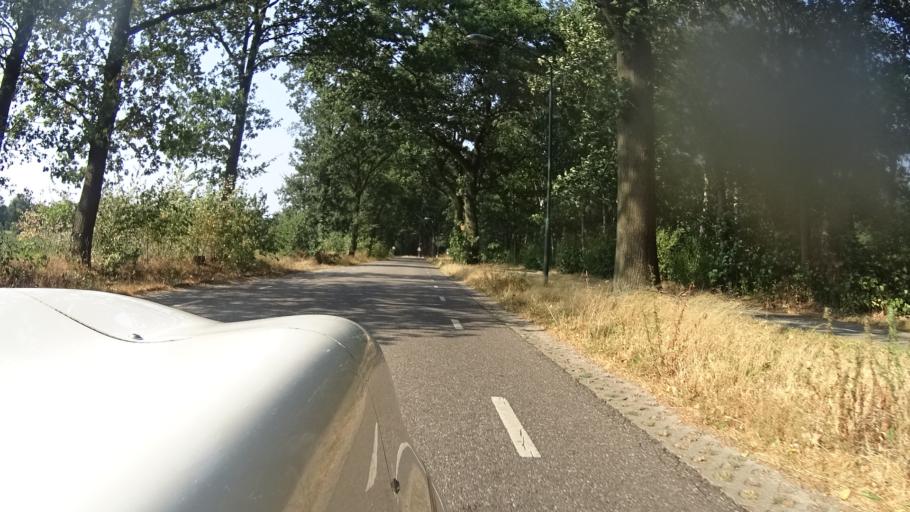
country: NL
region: North Brabant
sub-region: Gemeente Mill en Sint Hubert
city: Wilbertoord
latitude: 51.6634
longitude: 5.7739
